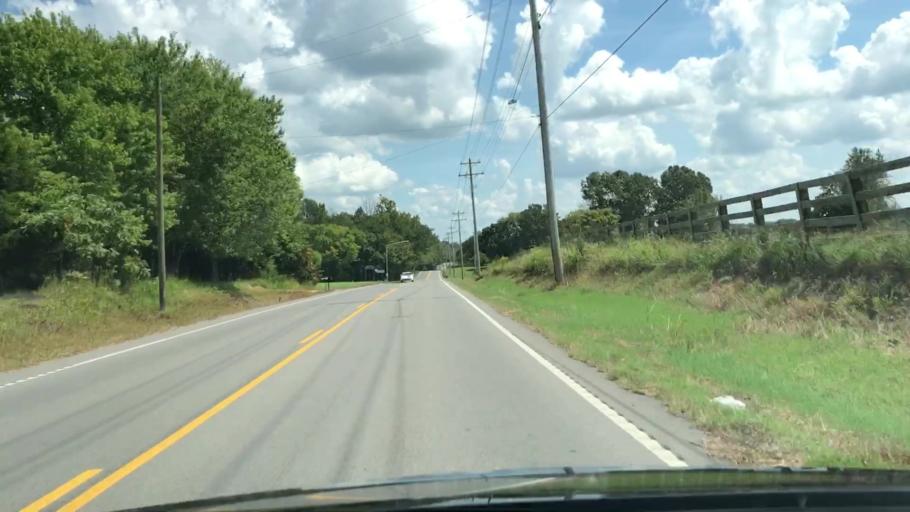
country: US
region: Tennessee
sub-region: Robertson County
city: Cross Plains
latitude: 36.5508
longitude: -86.7284
